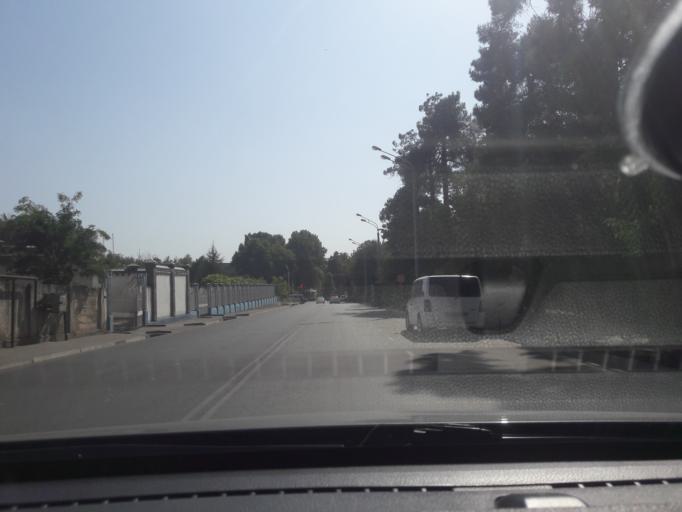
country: TJ
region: Dushanbe
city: Dushanbe
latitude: 38.5739
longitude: 68.8001
